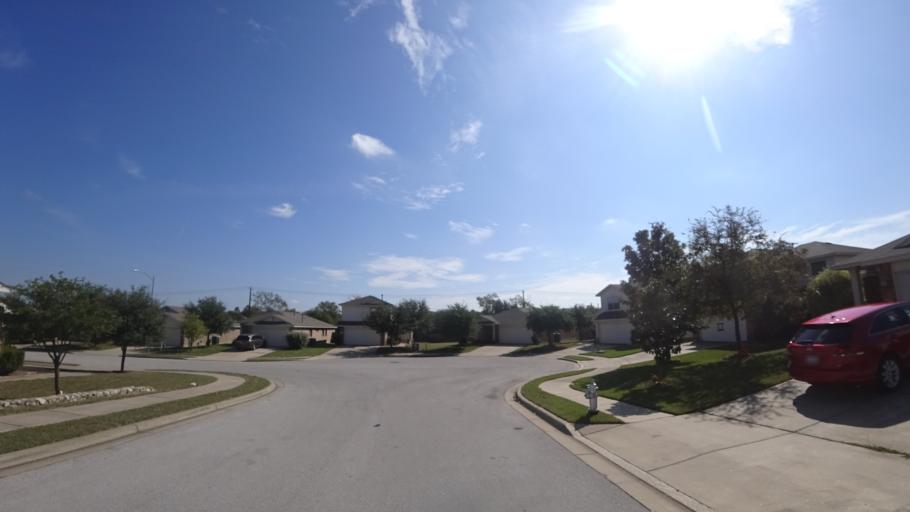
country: US
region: Texas
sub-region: Travis County
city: Pflugerville
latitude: 30.4198
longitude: -97.6306
